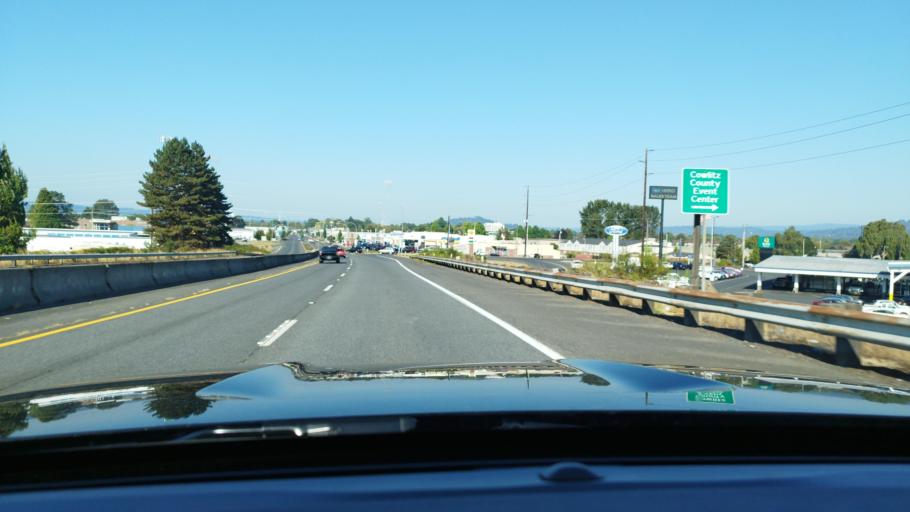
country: US
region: Washington
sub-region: Cowlitz County
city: Longview
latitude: 46.1239
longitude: -122.9285
